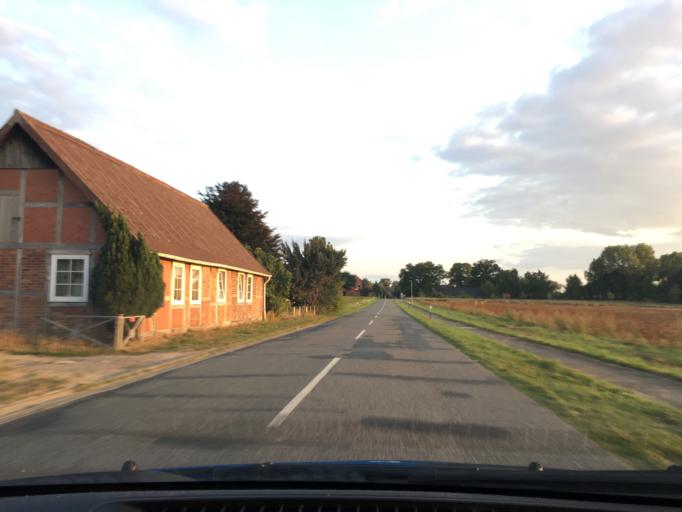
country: DE
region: Lower Saxony
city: Nahrendorf
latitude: 53.1789
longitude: 10.8157
